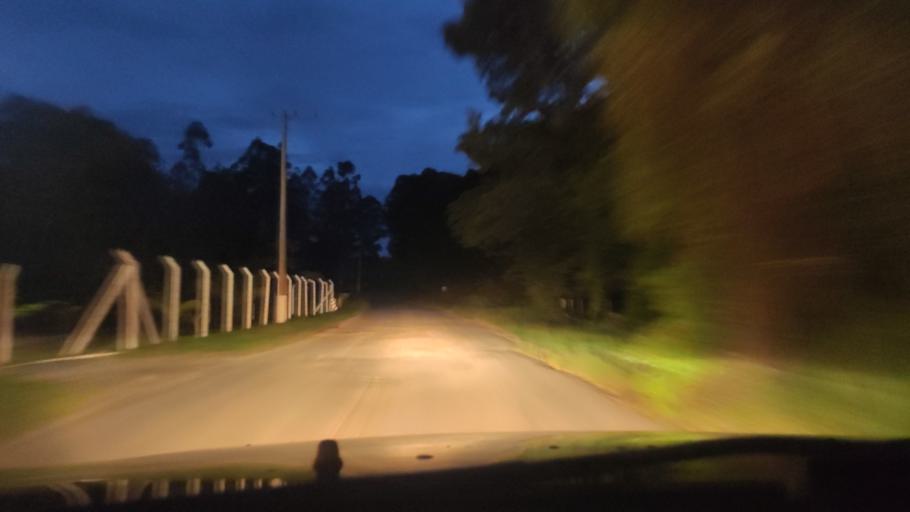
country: BR
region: Sao Paulo
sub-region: Serra Negra
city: Serra Negra
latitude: -22.5736
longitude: -46.6213
